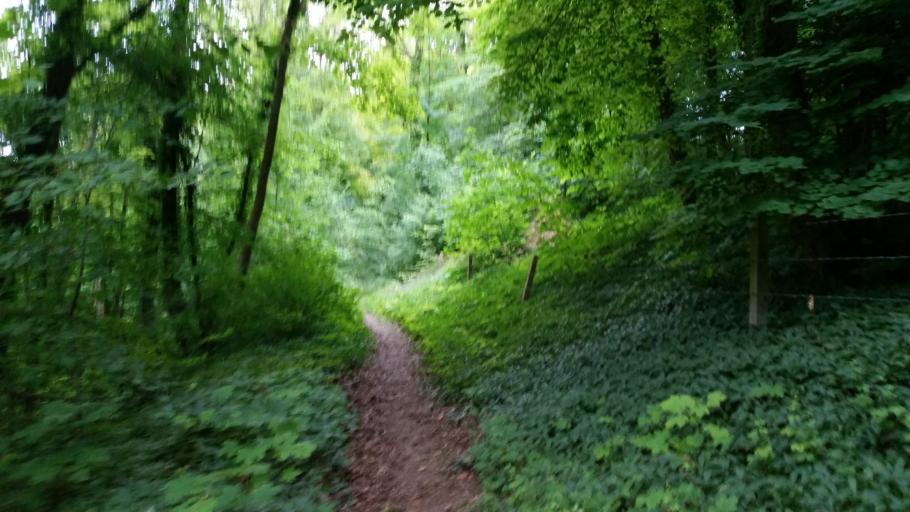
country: FR
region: Haute-Normandie
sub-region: Departement de la Seine-Maritime
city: Gaillefontaine
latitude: 49.6533
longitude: 1.6208
